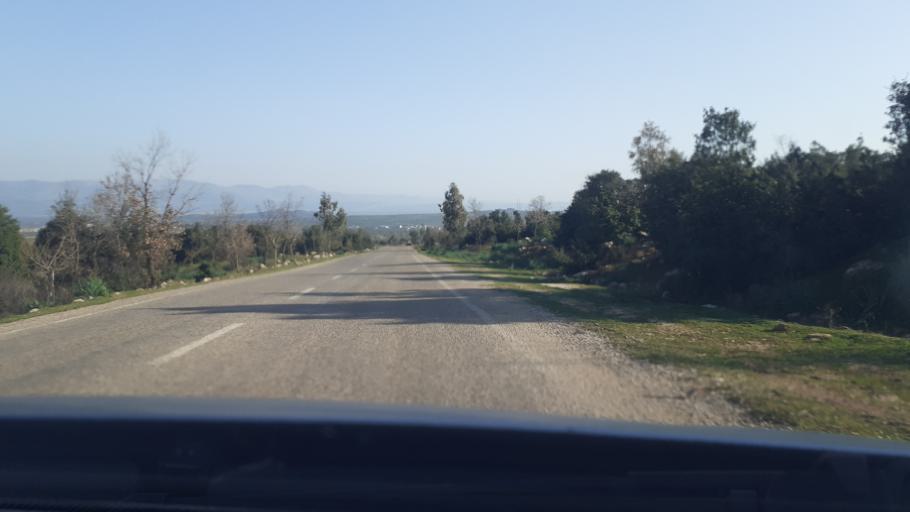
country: TR
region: Hatay
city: Aktepe
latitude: 36.7278
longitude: 36.4832
